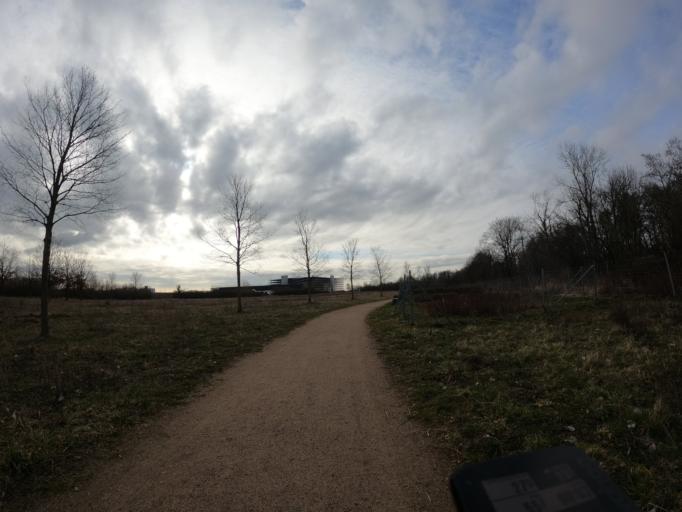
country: DE
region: Berlin
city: Altglienicke
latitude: 52.3930
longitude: 13.5333
